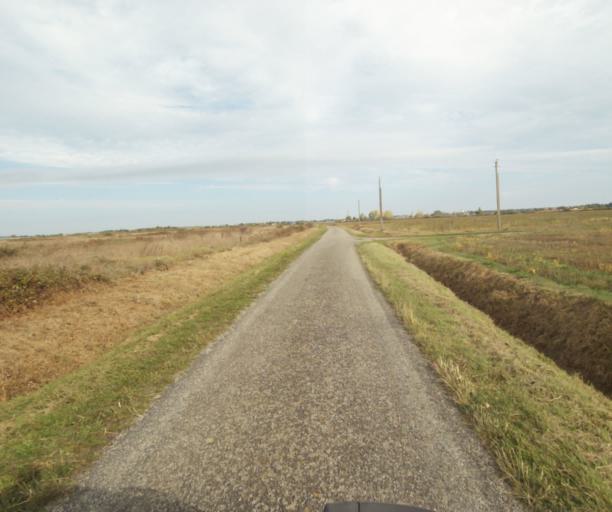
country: FR
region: Midi-Pyrenees
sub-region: Departement du Tarn-et-Garonne
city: Finhan
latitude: 43.9319
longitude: 1.2249
